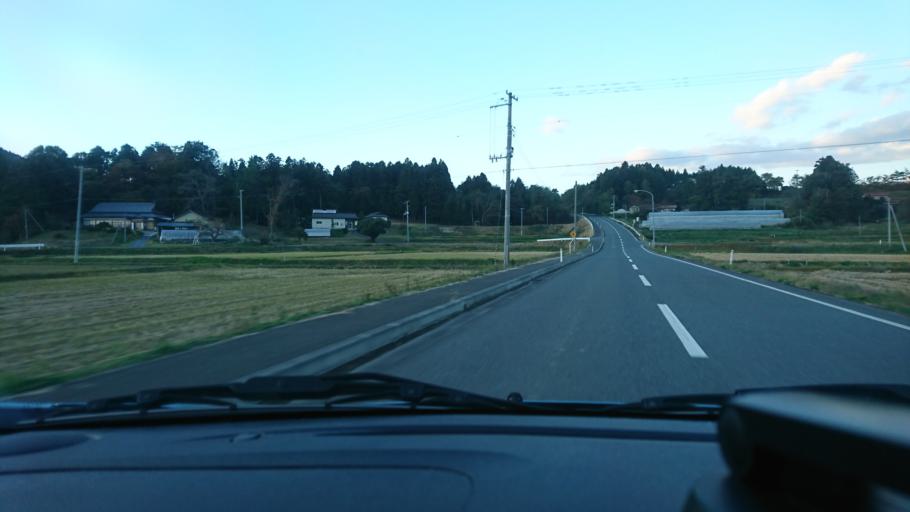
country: JP
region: Iwate
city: Ichinoseki
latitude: 38.7631
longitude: 141.2383
